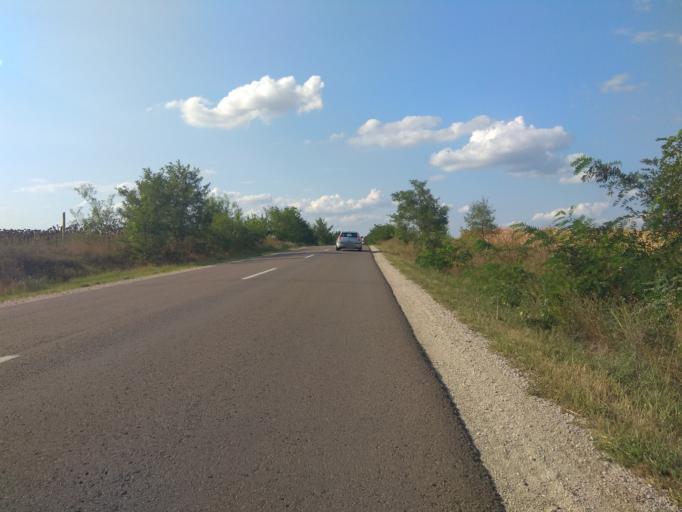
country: HU
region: Borsod-Abauj-Zemplen
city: Hejobaba
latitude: 47.9087
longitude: 20.8862
